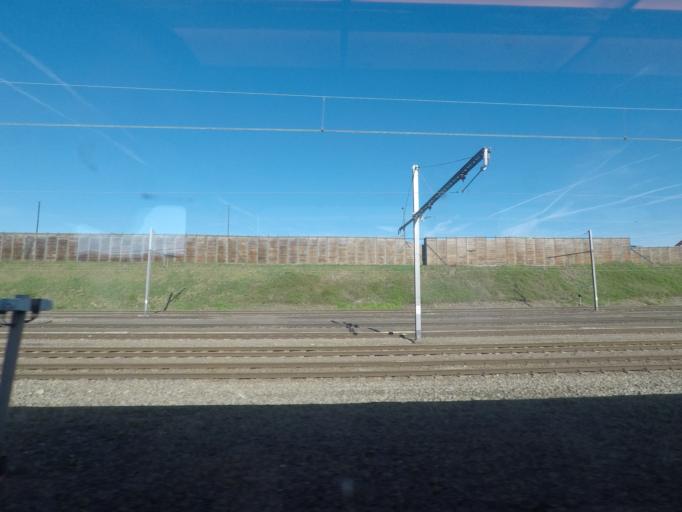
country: BE
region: Wallonia
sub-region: Province du Luxembourg
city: Marche-en-Famenne
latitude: 50.2009
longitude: 5.3117
